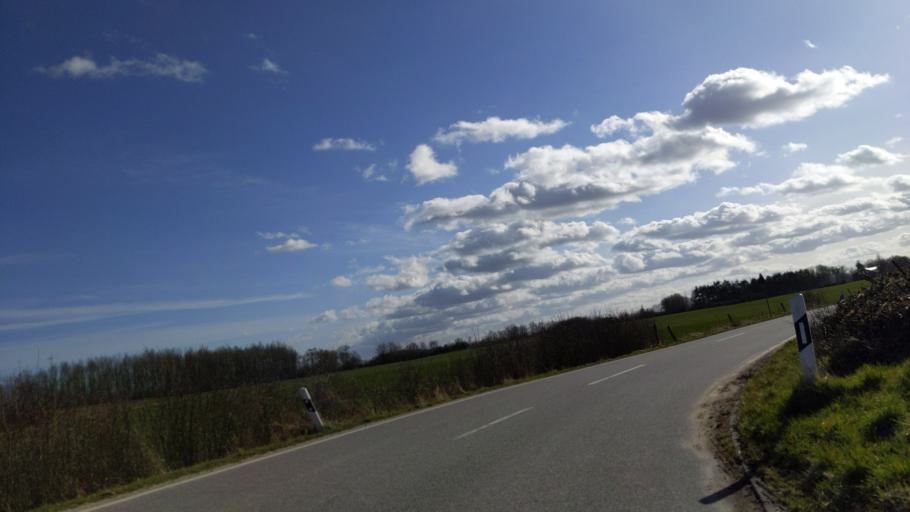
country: DE
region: Schleswig-Holstein
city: Travemuende
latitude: 53.9699
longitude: 10.8447
